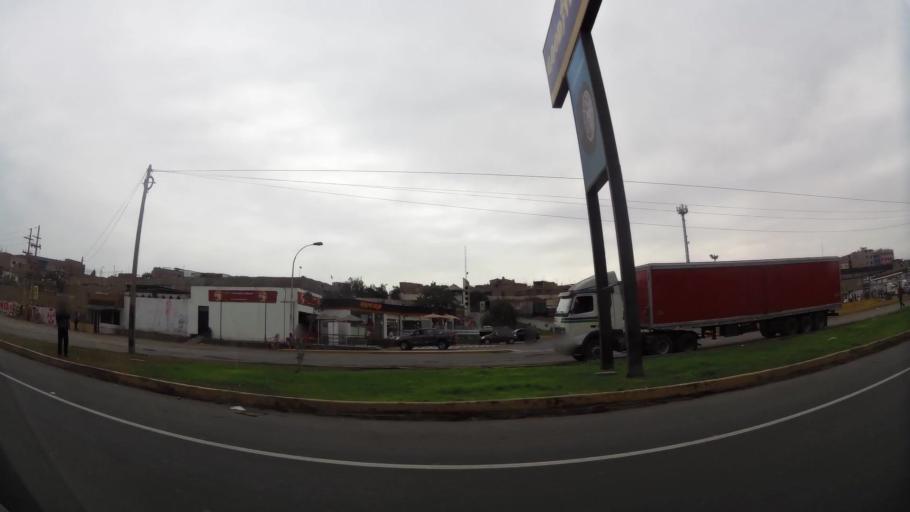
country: PE
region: Lima
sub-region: Lima
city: Surco
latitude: -12.2004
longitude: -76.9739
